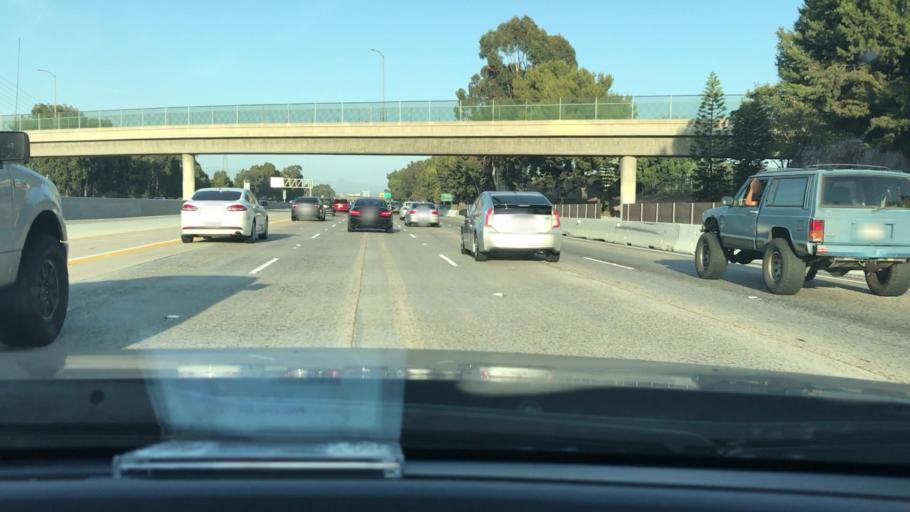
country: US
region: California
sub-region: Orange County
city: Irvine
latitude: 33.6643
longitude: -117.8078
